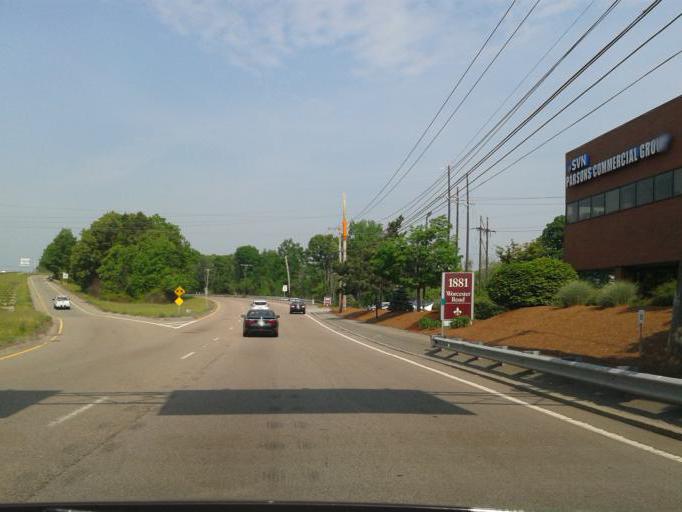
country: US
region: Massachusetts
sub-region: Worcester County
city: Southborough
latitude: 42.2974
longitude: -71.4855
